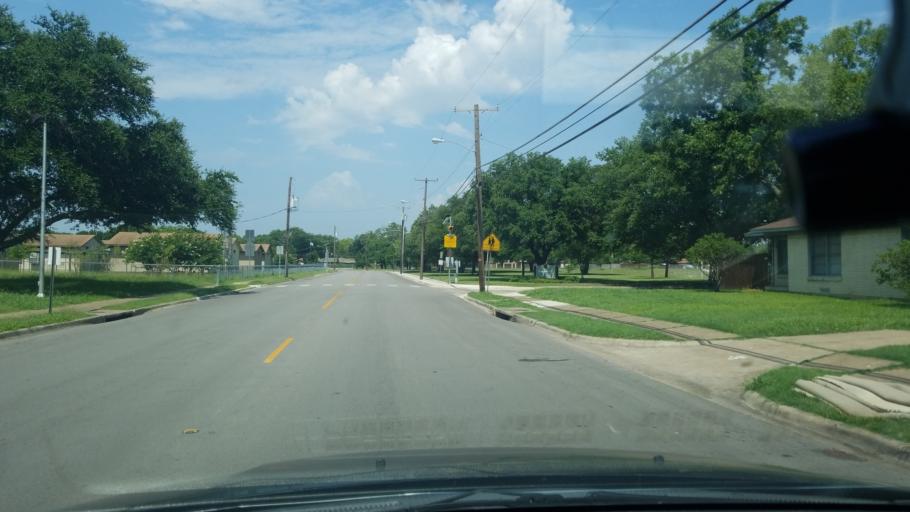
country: US
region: Texas
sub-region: Dallas County
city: Balch Springs
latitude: 32.7428
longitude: -96.6883
